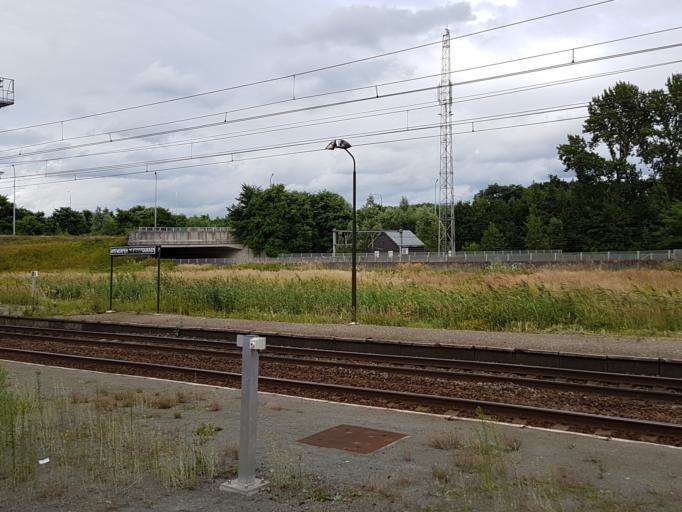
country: BE
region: Flanders
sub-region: Provincie Antwerpen
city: Antwerpen
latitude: 51.2619
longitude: 4.4279
